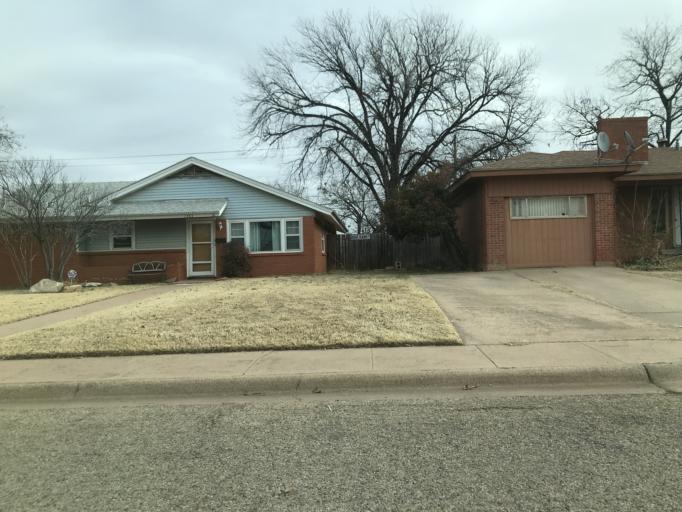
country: US
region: Texas
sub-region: Taylor County
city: Abilene
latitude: 32.4652
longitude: -99.7611
